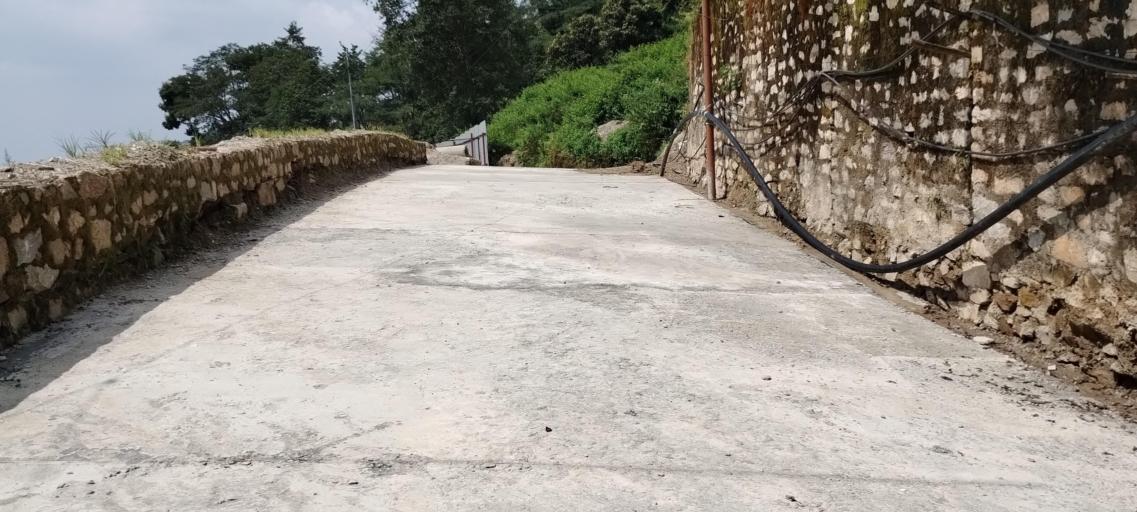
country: NP
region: Central Region
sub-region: Bagmati Zone
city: Kathmandu
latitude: 27.7899
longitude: 85.3639
